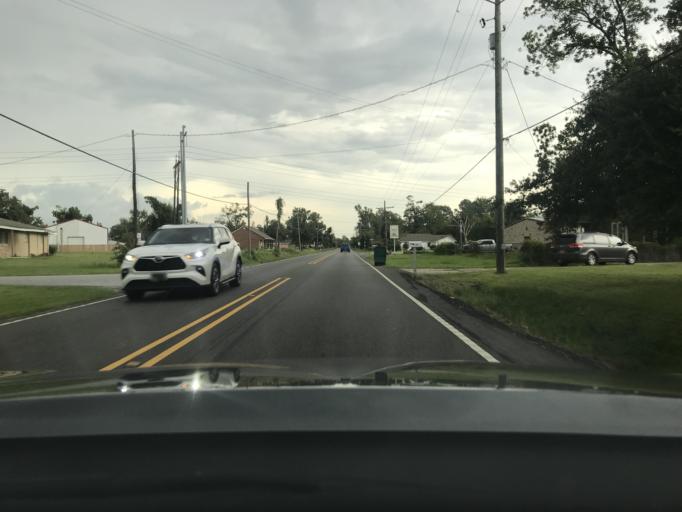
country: US
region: Louisiana
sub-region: Calcasieu Parish
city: Westlake
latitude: 30.2652
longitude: -93.2453
